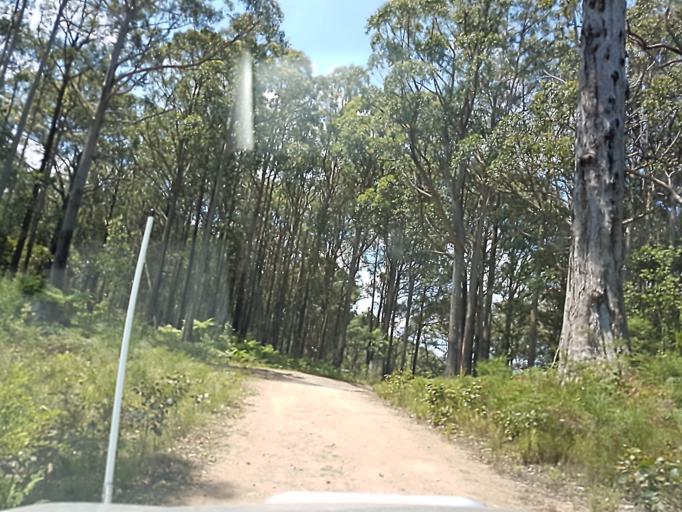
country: AU
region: Victoria
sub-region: East Gippsland
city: Lakes Entrance
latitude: -37.3868
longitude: 148.2900
